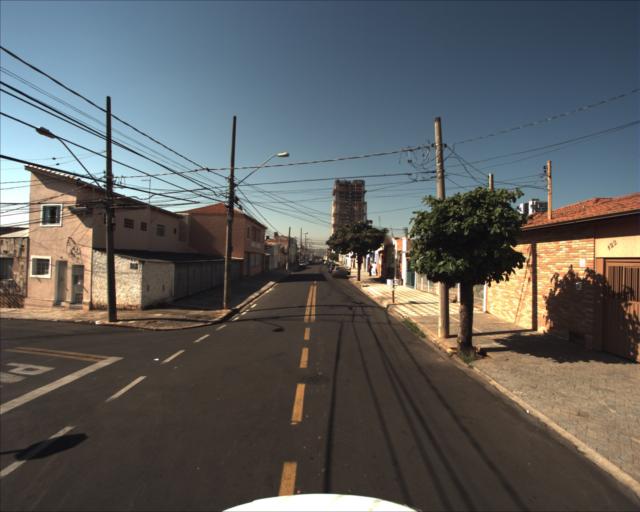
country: BR
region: Sao Paulo
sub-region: Sorocaba
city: Sorocaba
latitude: -23.5036
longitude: -47.4450
